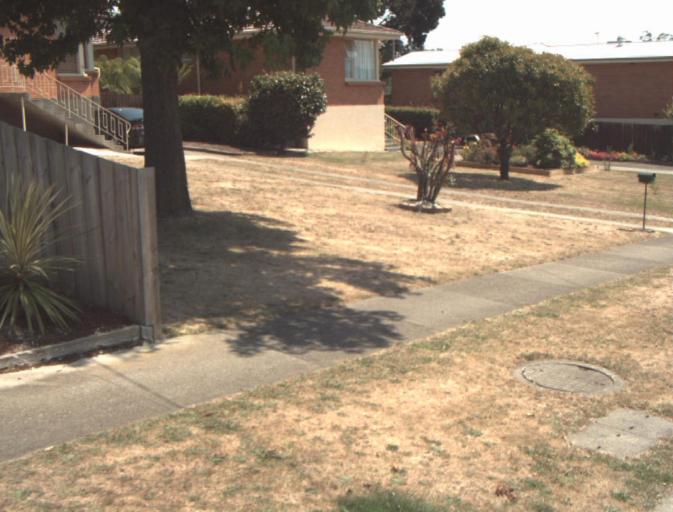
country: AU
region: Tasmania
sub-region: Launceston
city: Summerhill
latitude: -41.4867
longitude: 147.1746
